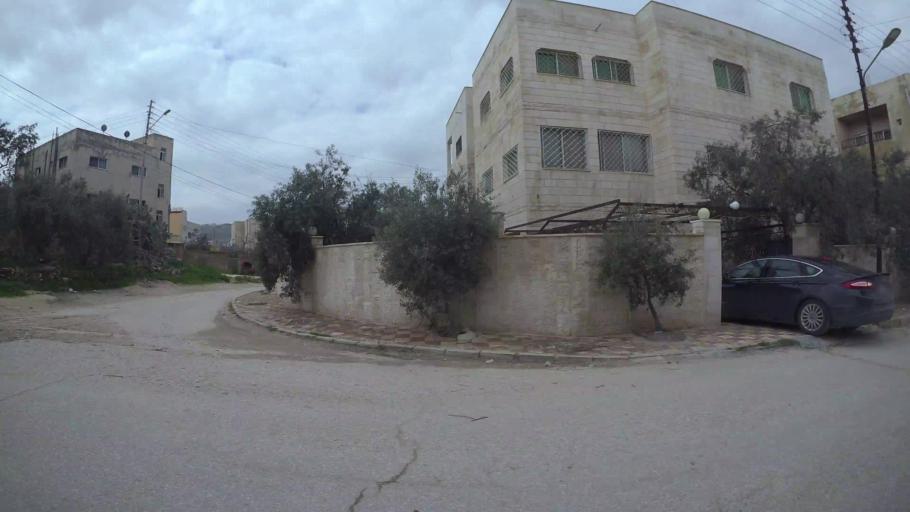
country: JO
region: Amman
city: Al Jubayhah
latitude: 32.0577
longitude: 35.8238
